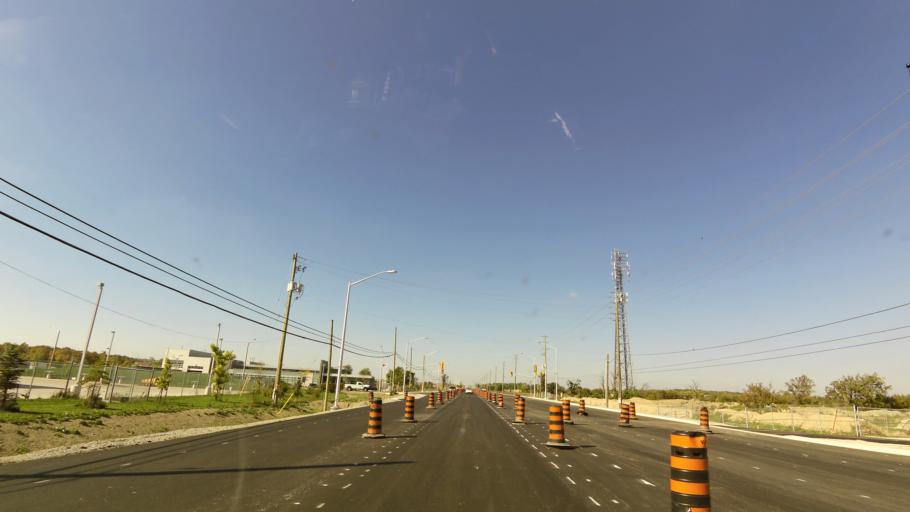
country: CA
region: Ontario
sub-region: Halton
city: Milton
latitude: 43.4817
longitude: -79.8277
